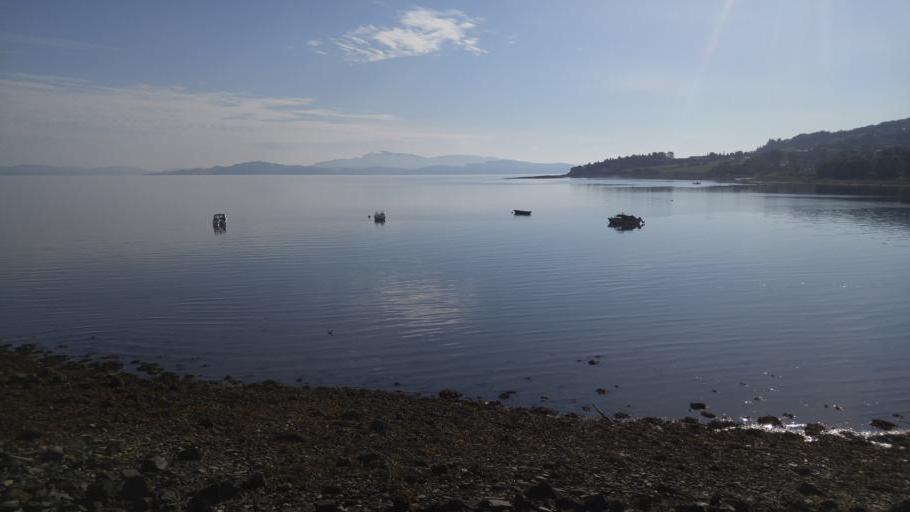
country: NO
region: Sor-Trondelag
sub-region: Malvik
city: Malvik
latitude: 63.4386
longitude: 10.6094
